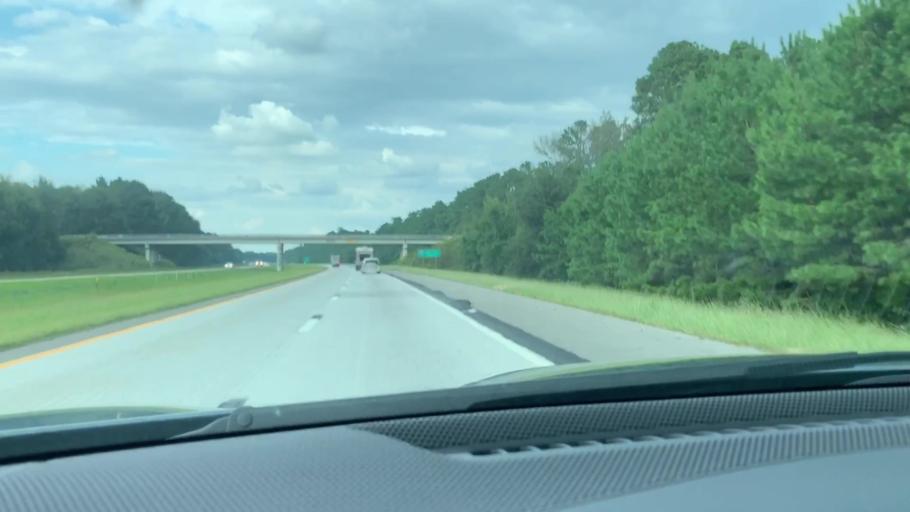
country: US
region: South Carolina
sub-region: Dorchester County
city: Saint George
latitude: 33.2939
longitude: -80.5580
